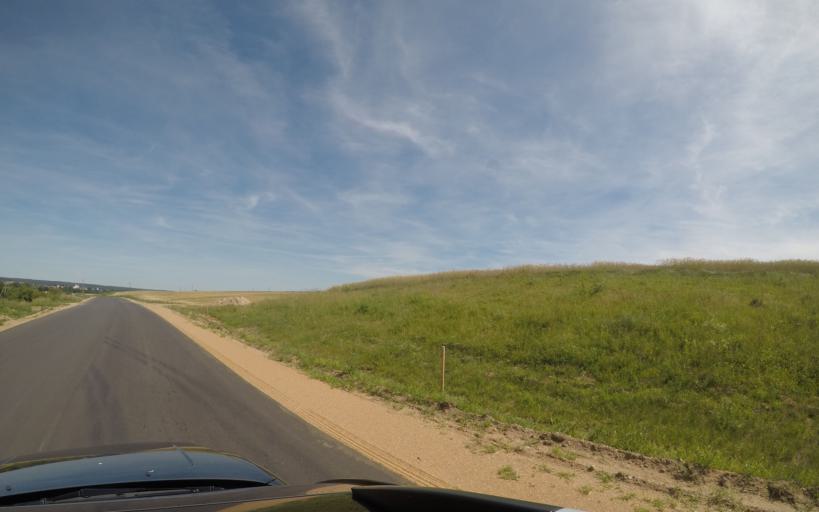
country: BY
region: Grodnenskaya
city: Hal'shany
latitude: 54.2583
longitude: 25.9799
